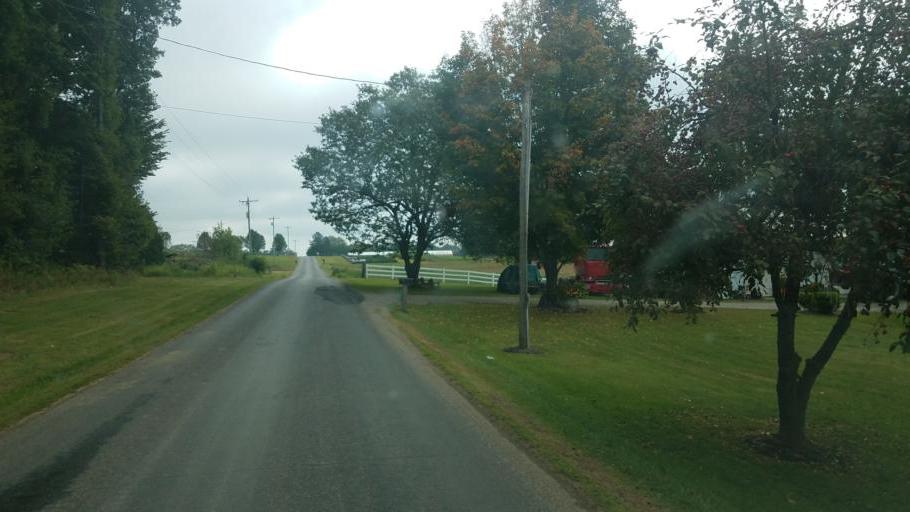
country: US
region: Ohio
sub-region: Licking County
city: Utica
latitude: 40.2559
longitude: -82.3703
